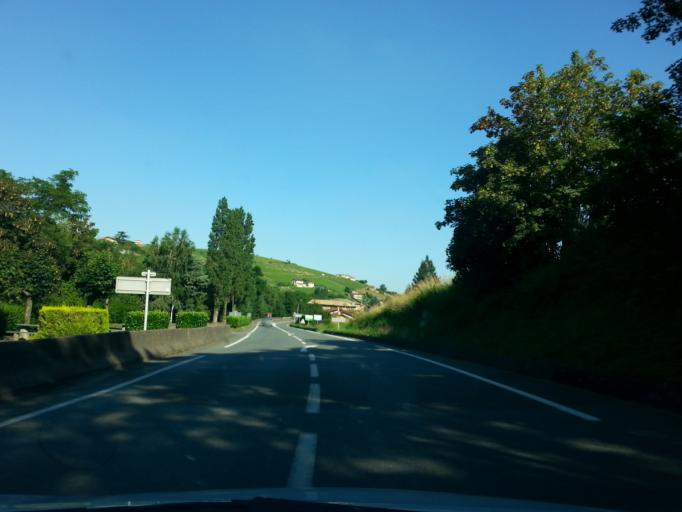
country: FR
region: Rhone-Alpes
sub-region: Departement du Rhone
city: Beaujeu
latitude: 46.1504
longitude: 4.5922
